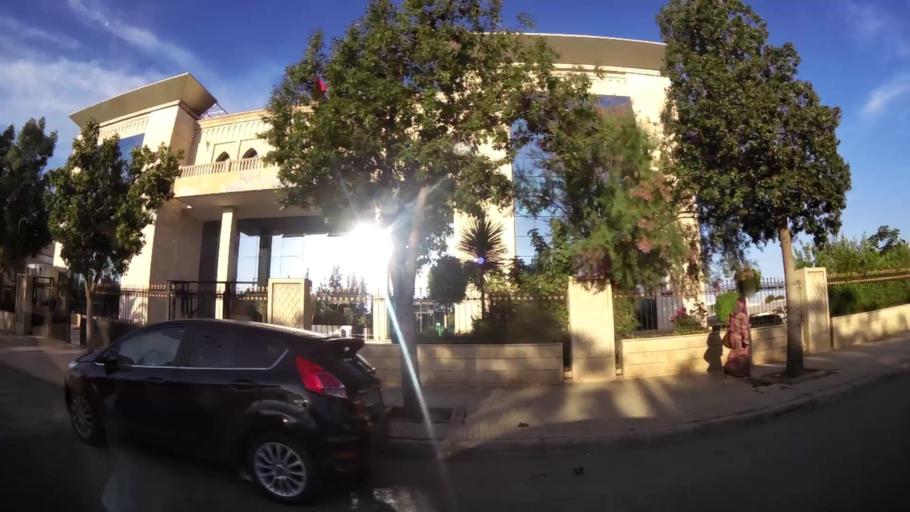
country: MA
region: Oriental
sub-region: Oujda-Angad
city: Oujda
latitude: 34.6978
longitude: -1.9191
